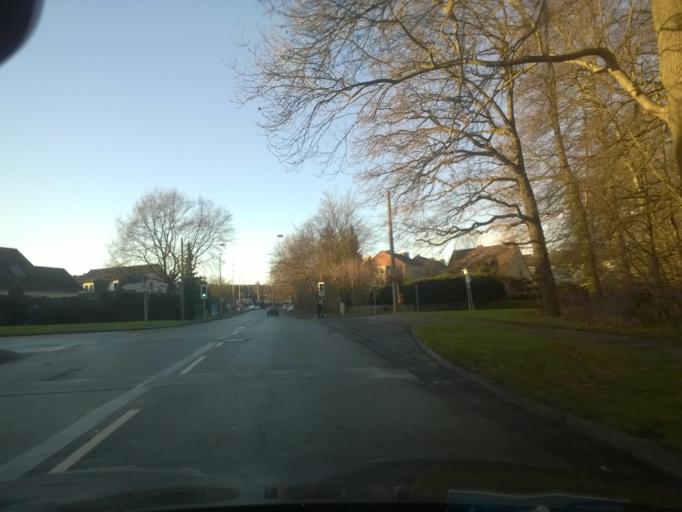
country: DE
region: Lower Saxony
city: Hildesheim
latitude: 52.1419
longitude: 9.9260
